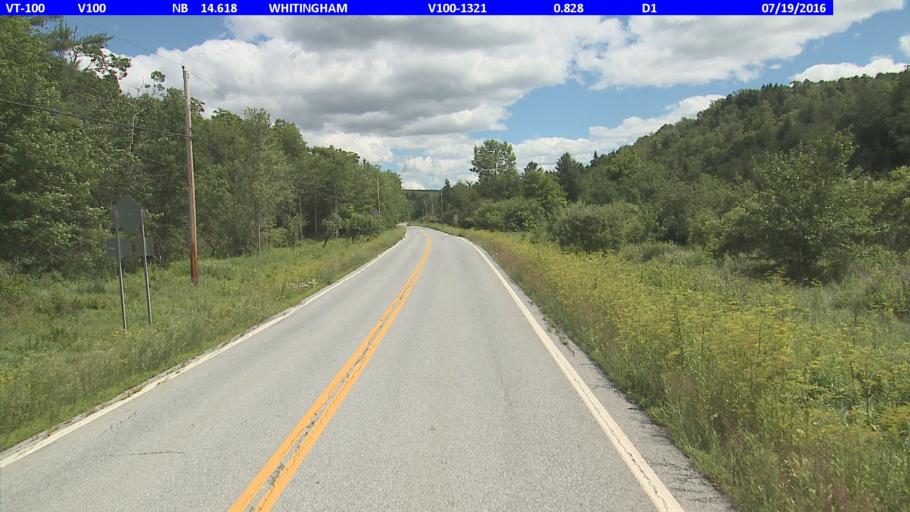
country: US
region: Massachusetts
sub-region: Franklin County
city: Charlemont
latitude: 42.7689
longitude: -72.9146
